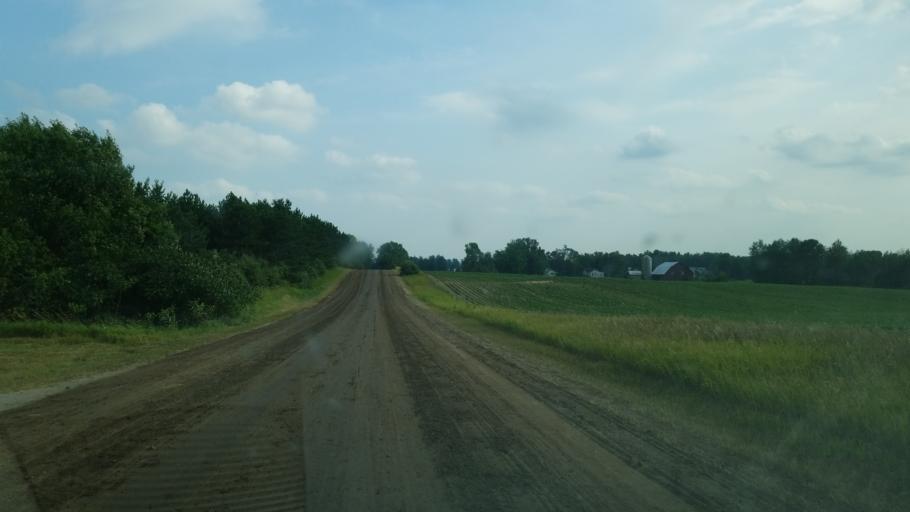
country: US
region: Michigan
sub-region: Mecosta County
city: Canadian Lakes
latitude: 43.5584
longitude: -85.3636
